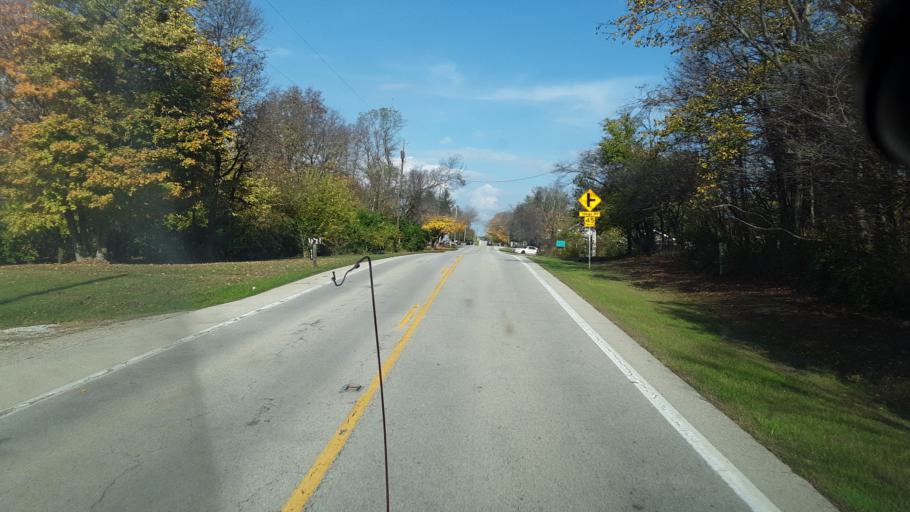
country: US
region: Ohio
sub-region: Clinton County
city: Sabina
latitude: 39.5353
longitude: -83.7048
